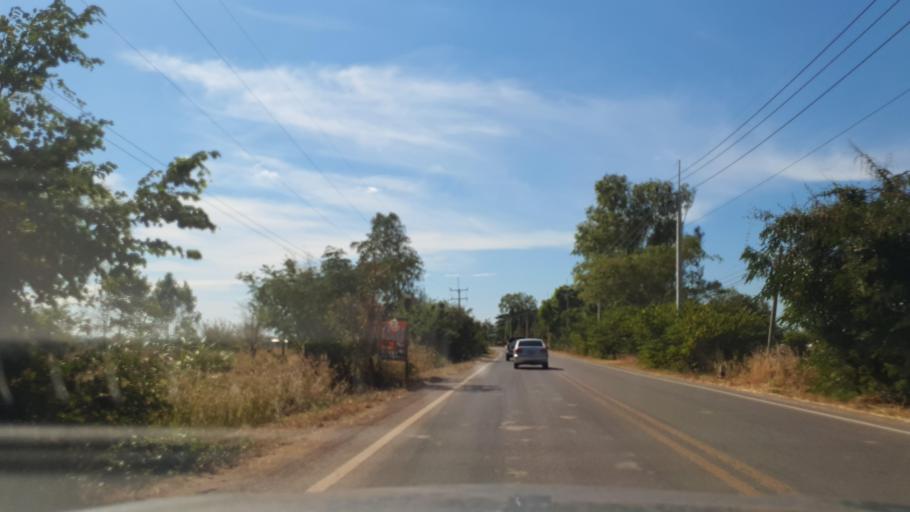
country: TH
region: Kalasin
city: Khao Wong
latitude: 16.7474
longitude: 104.1158
